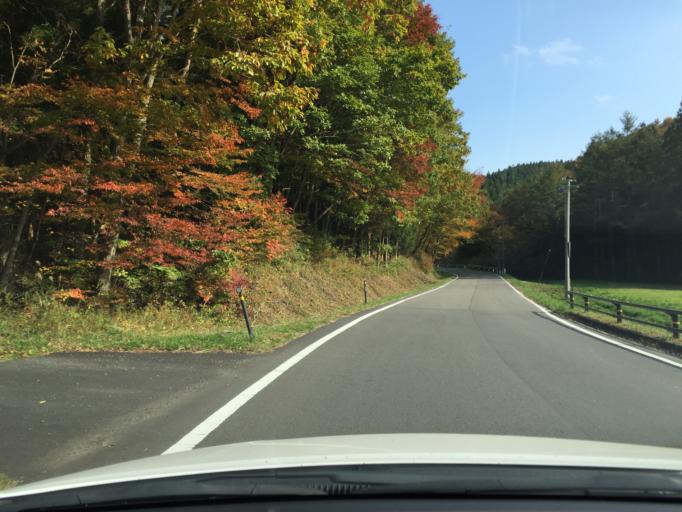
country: JP
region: Fukushima
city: Ishikawa
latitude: 36.9557
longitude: 140.5605
